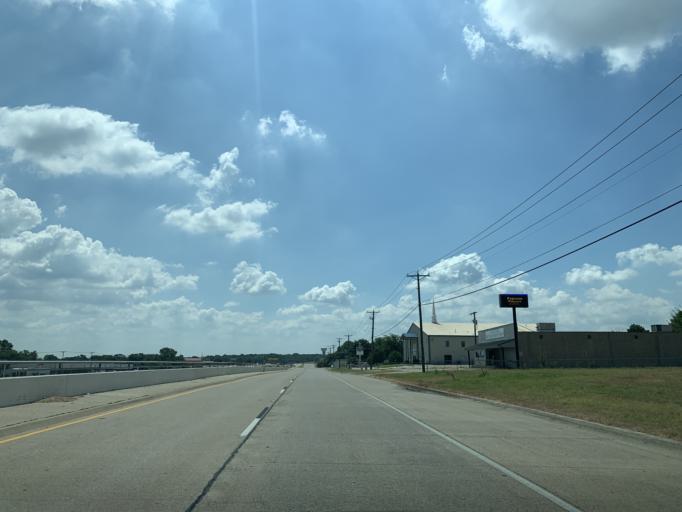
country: US
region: Texas
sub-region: Tarrant County
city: Azle
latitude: 32.8767
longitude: -97.5321
